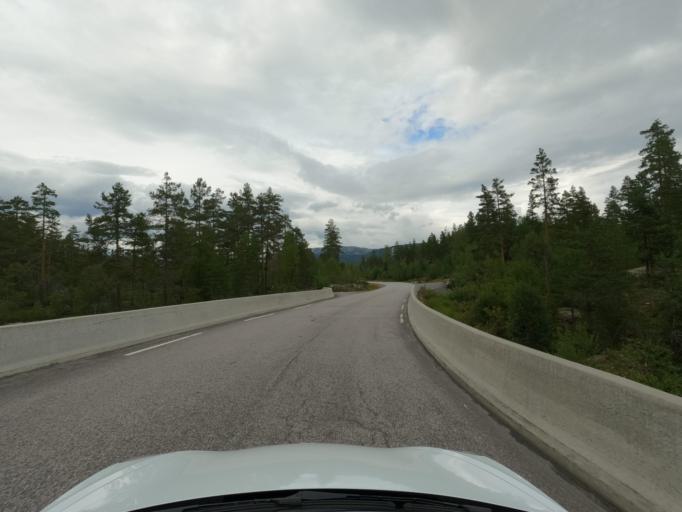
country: NO
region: Telemark
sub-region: Notodden
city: Notodden
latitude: 59.7069
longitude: 9.1506
